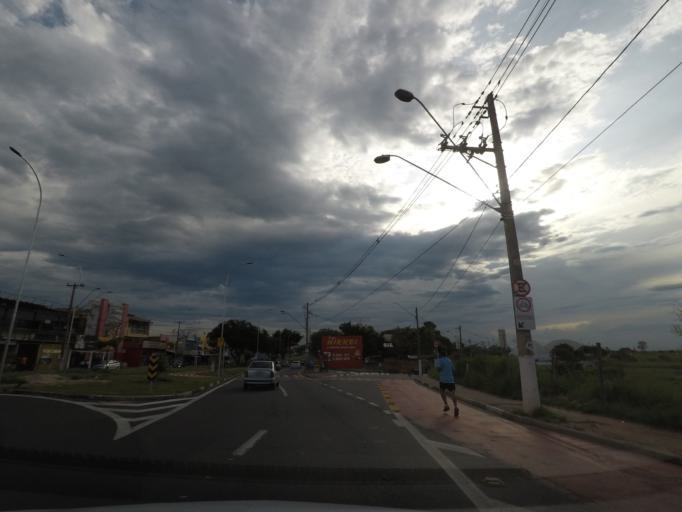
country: BR
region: Sao Paulo
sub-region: Hortolandia
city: Hortolandia
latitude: -22.9508
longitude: -47.1877
